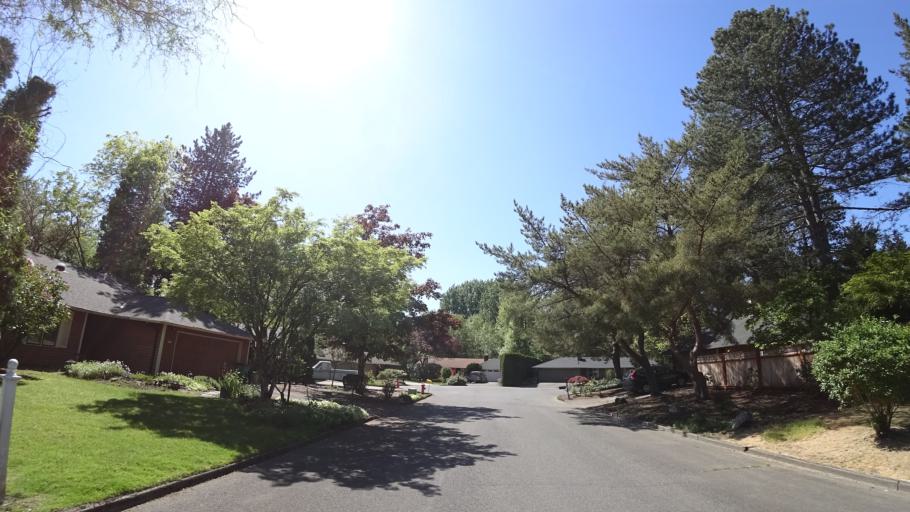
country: US
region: Oregon
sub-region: Washington County
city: Raleigh Hills
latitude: 45.4887
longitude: -122.7364
